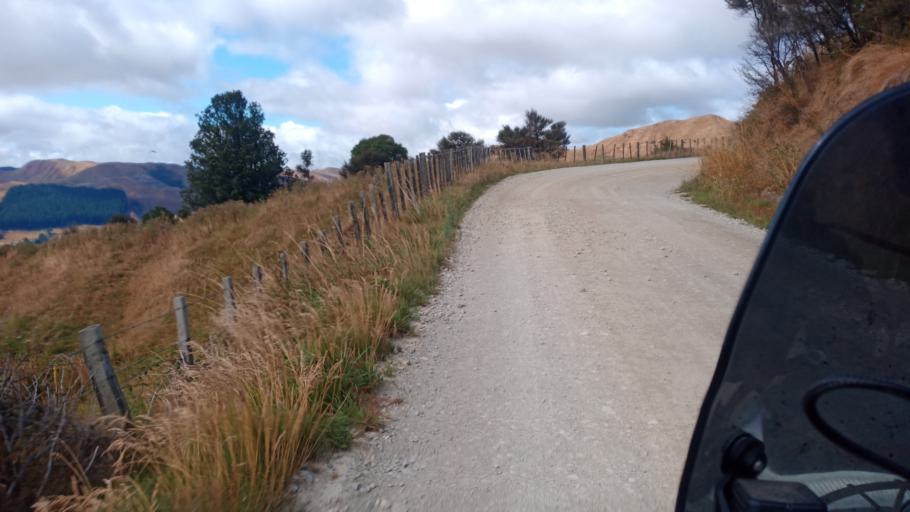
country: NZ
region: Hawke's Bay
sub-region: Wairoa District
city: Wairoa
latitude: -38.6043
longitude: 177.4686
